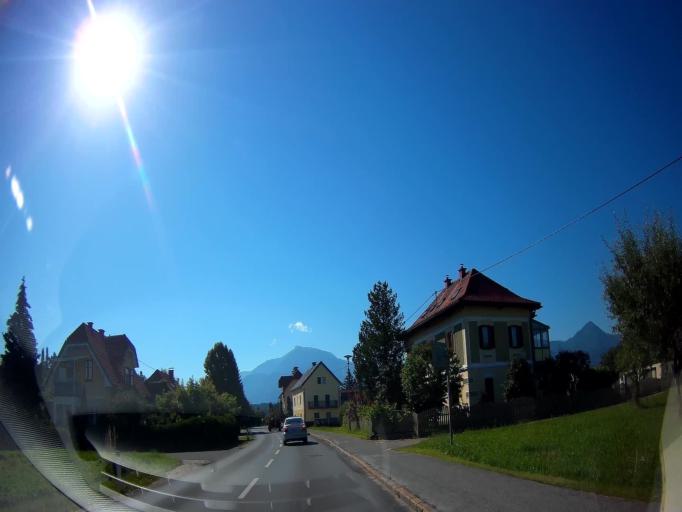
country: AT
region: Carinthia
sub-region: Politischer Bezirk Volkermarkt
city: Eberndorf
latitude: 46.5889
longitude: 14.6450
